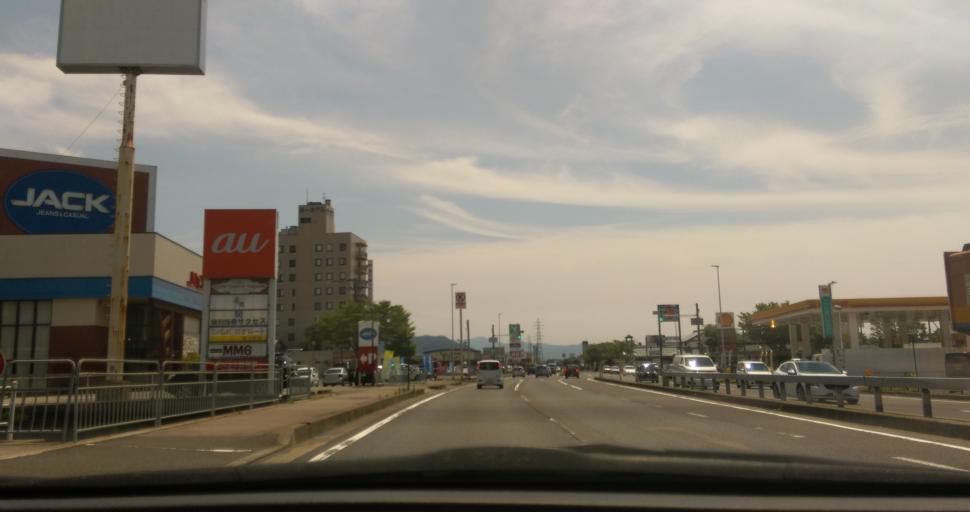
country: JP
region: Fukui
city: Sabae
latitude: 35.9439
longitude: 136.1941
